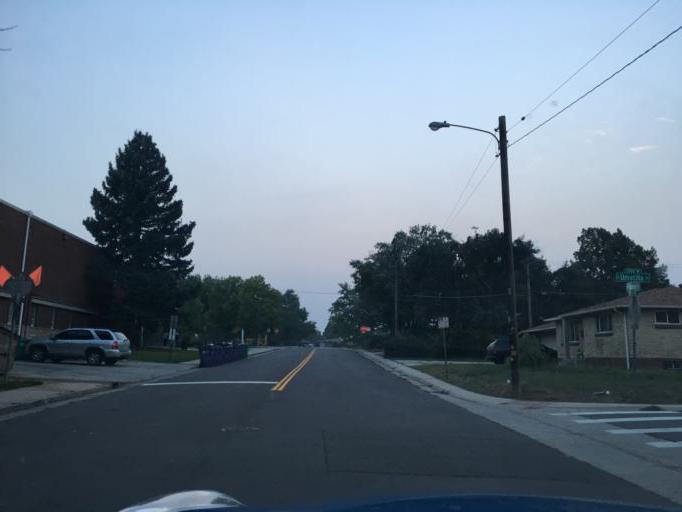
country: US
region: Colorado
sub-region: Arapahoe County
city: Sheridan
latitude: 39.6909
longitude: -105.0125
